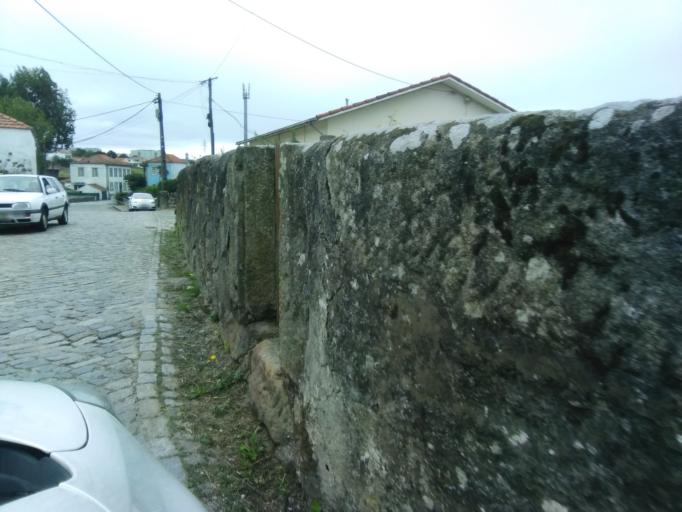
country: PT
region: Porto
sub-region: Matosinhos
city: Santa Cruz do Bispo
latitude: 41.2272
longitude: -8.7058
